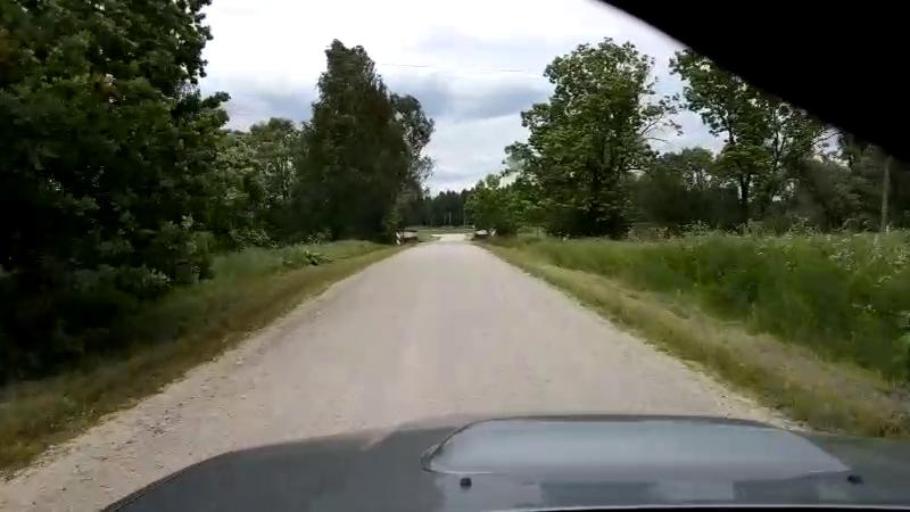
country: EE
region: Paernumaa
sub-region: Halinga vald
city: Parnu-Jaagupi
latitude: 58.5143
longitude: 24.5808
